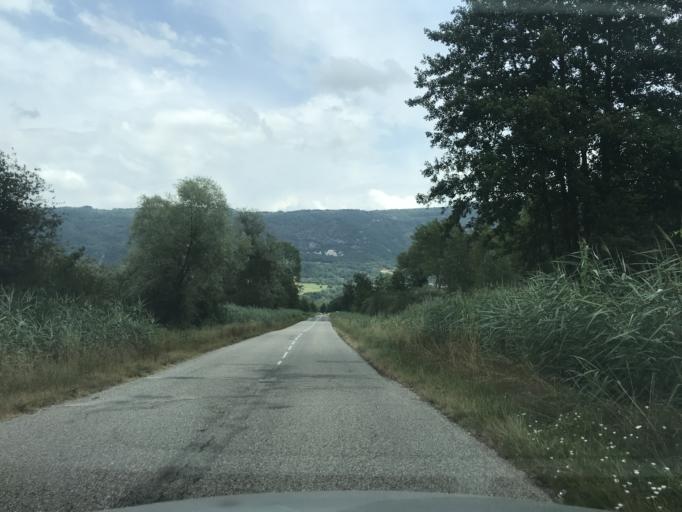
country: FR
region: Rhone-Alpes
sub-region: Departement de la Savoie
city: Chindrieux
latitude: 45.8290
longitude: 5.8210
